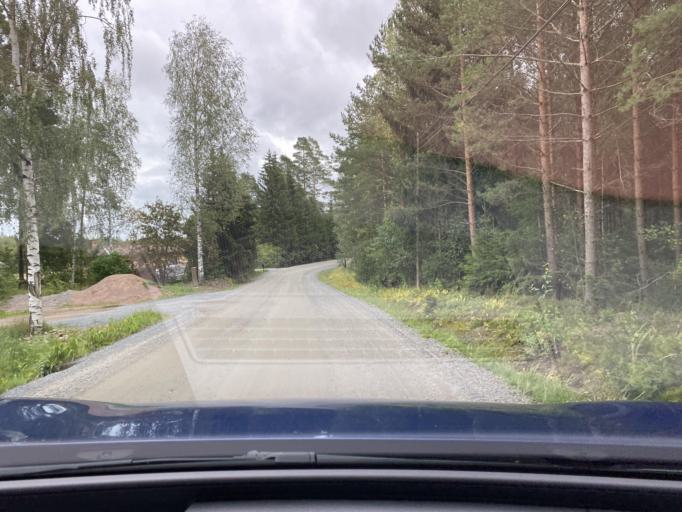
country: FI
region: Pirkanmaa
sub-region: Lounais-Pirkanmaa
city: Vammala
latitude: 61.2709
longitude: 22.9631
